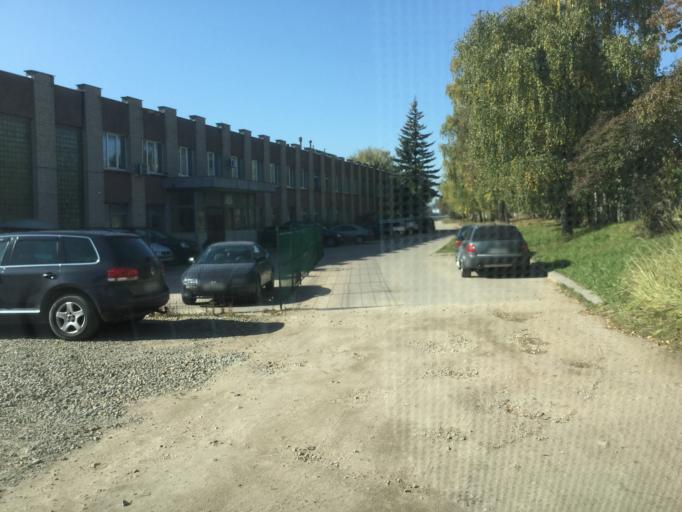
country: BY
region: Vitebsk
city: Vitebsk
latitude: 55.1818
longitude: 30.2537
